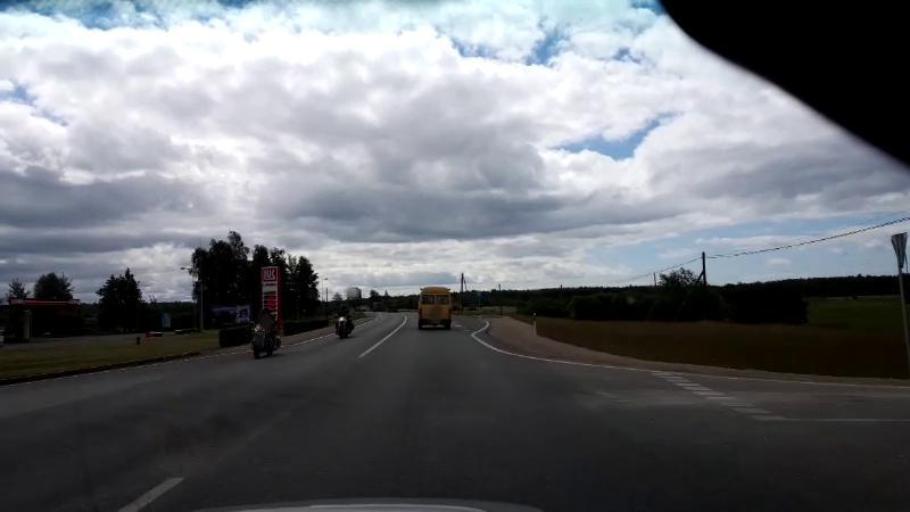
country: LV
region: Salacgrivas
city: Salacgriva
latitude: 57.7405
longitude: 24.3619
